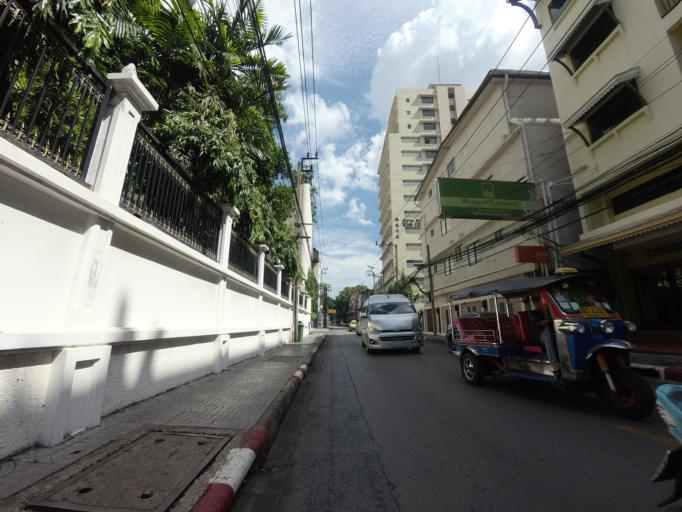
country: TH
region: Bangkok
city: Khlong Toei
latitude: 13.7356
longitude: 100.5531
